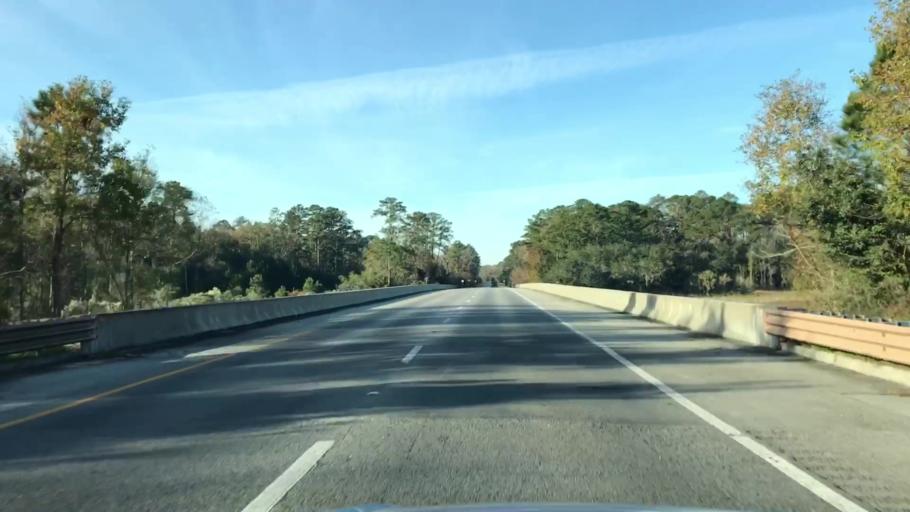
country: US
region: South Carolina
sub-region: Hampton County
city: Yemassee
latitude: 32.6484
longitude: -80.6963
